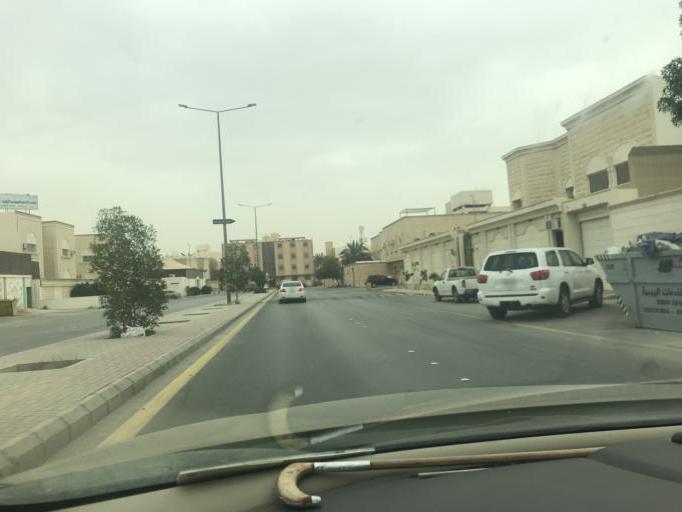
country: SA
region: Ar Riyad
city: Riyadh
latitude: 24.7383
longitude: 46.7543
